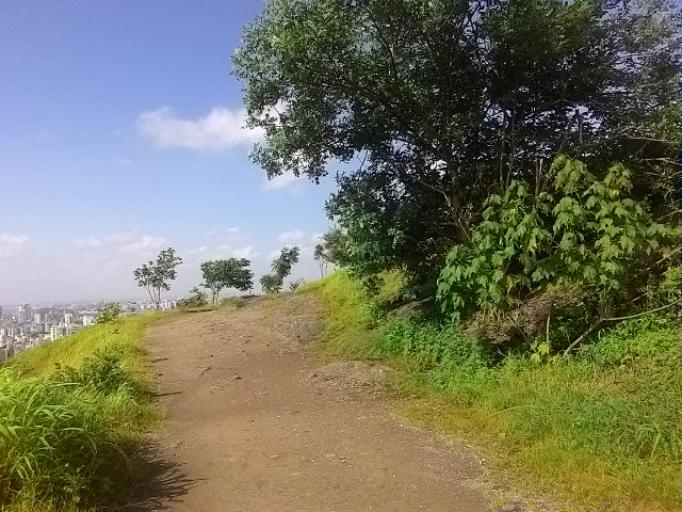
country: IN
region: Maharashtra
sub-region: Pune Division
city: Khadki
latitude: 18.5478
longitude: 73.7751
